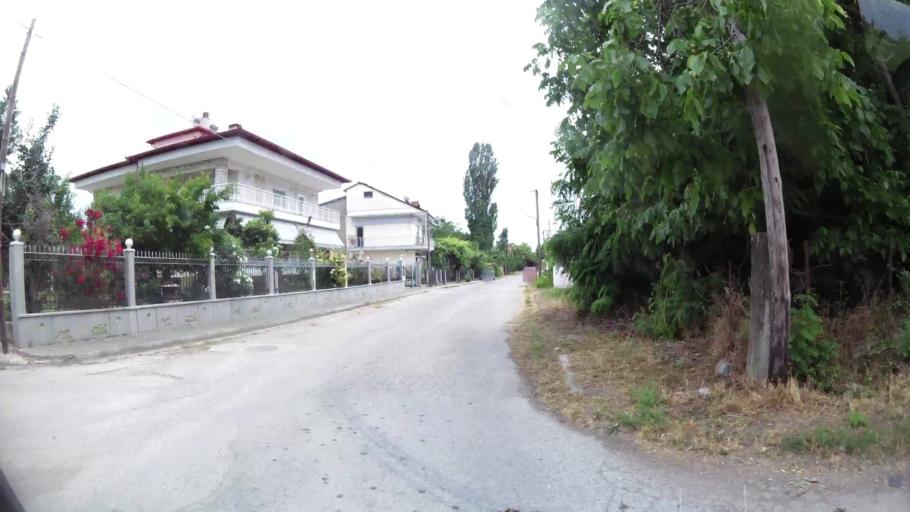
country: GR
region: Central Macedonia
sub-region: Nomos Pierias
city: Kallithea
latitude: 40.2754
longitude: 22.5706
